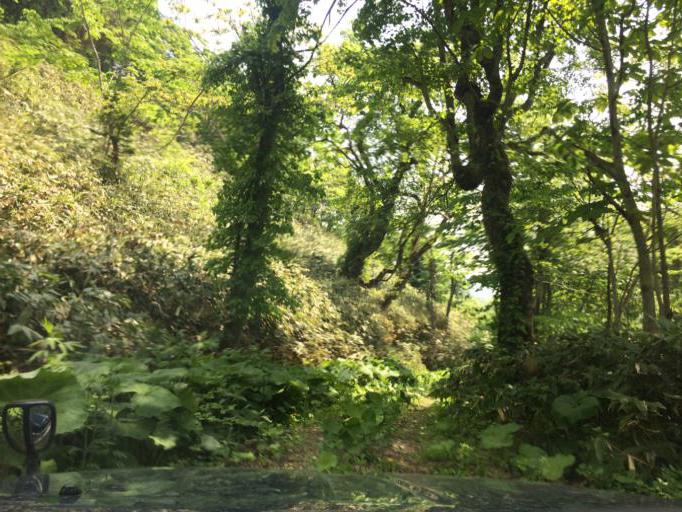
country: JP
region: Hokkaido
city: Niseko Town
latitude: 42.7162
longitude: 140.5458
